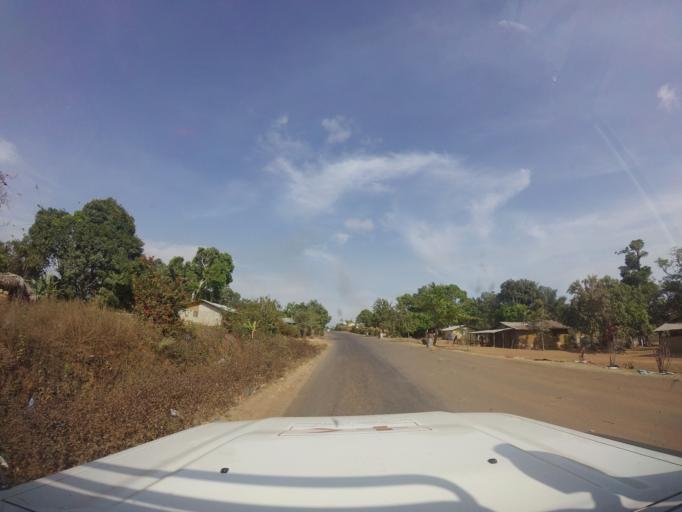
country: LR
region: Bomi
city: Tubmanburg
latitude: 6.7020
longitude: -10.9185
